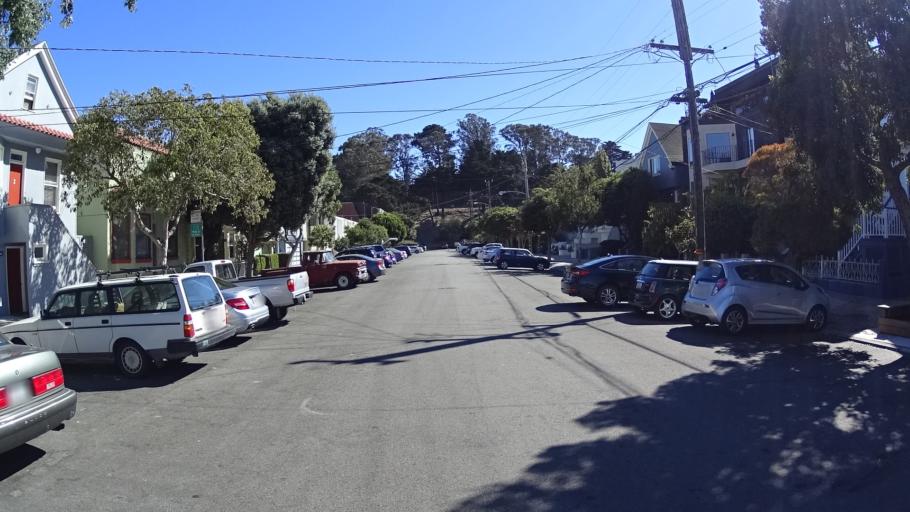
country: US
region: California
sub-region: San Francisco County
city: San Francisco
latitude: 37.7586
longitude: -122.3971
